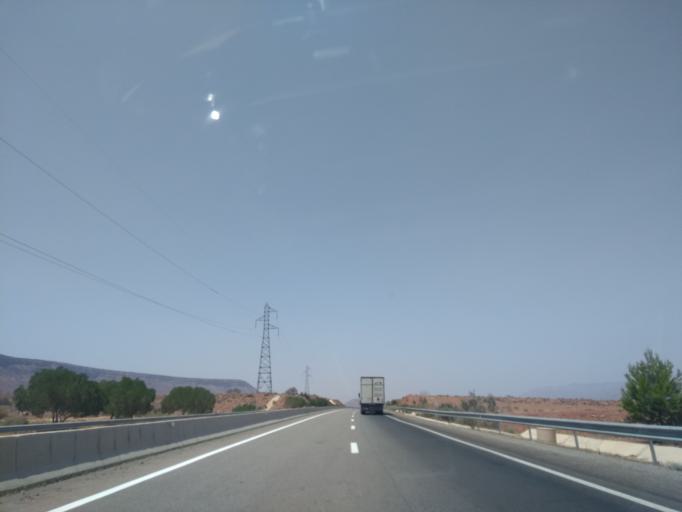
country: MA
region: Marrakech-Tensift-Al Haouz
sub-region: Chichaoua
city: Timezgadiouine
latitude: 30.8916
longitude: -9.0769
